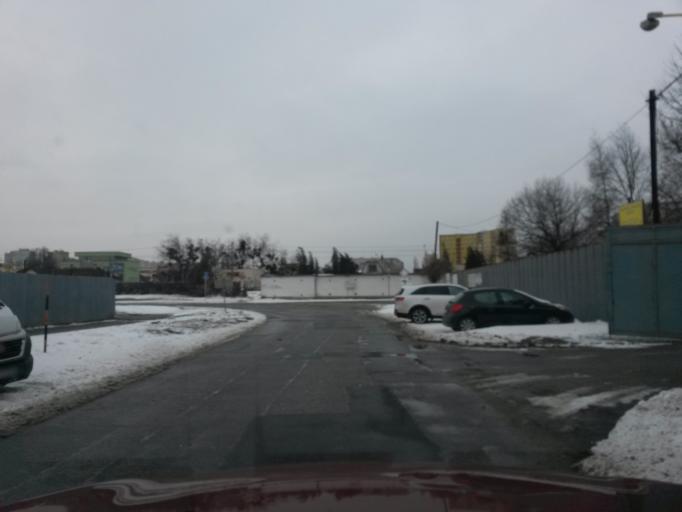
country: SK
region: Kosicky
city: Kosice
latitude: 48.7093
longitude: 21.2672
